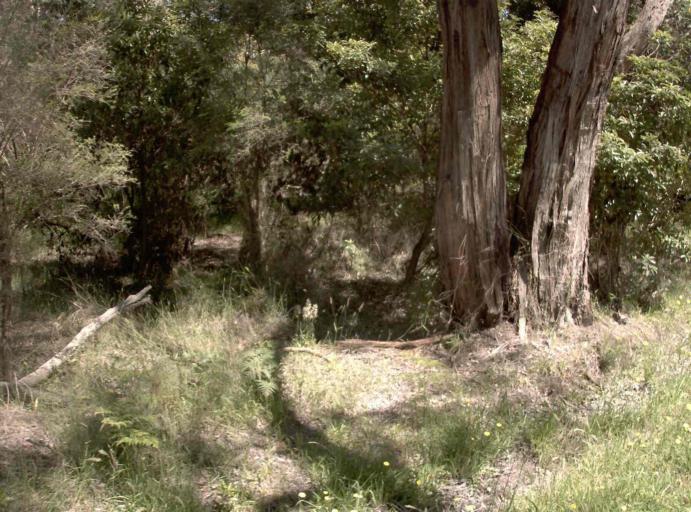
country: AU
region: Victoria
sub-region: Bass Coast
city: North Wonthaggi
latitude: -38.7576
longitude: 146.0717
